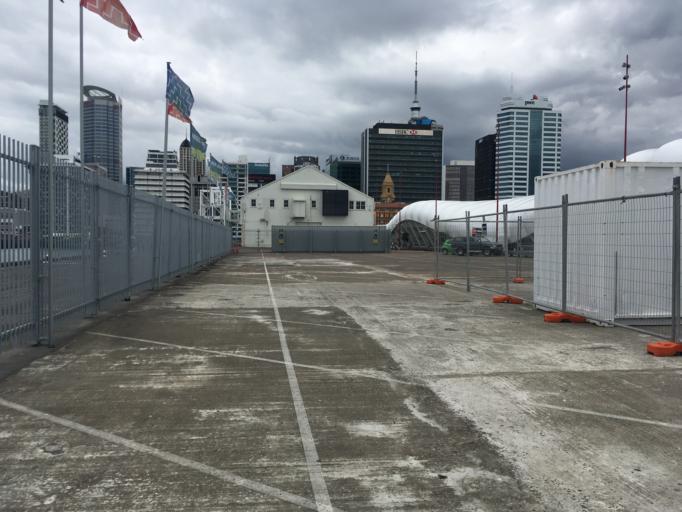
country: NZ
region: Auckland
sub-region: Auckland
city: Auckland
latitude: -36.8403
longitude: 174.7689
